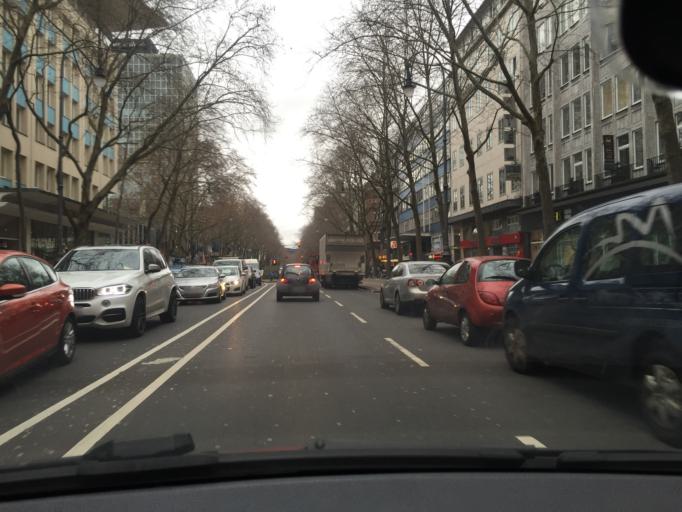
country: DE
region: North Rhine-Westphalia
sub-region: Regierungsbezirk Koln
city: Koeln
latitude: 50.9373
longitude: 6.9391
